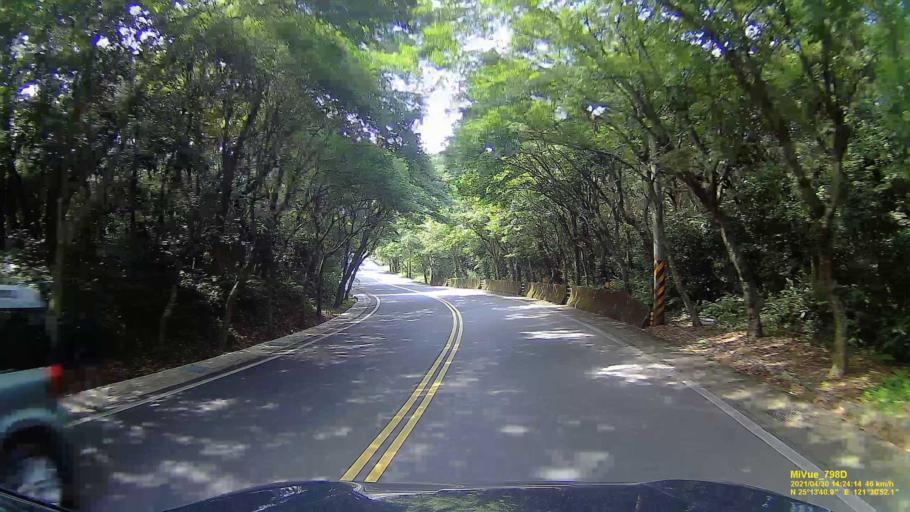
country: TW
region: Taipei
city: Taipei
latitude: 25.2283
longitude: 121.5143
